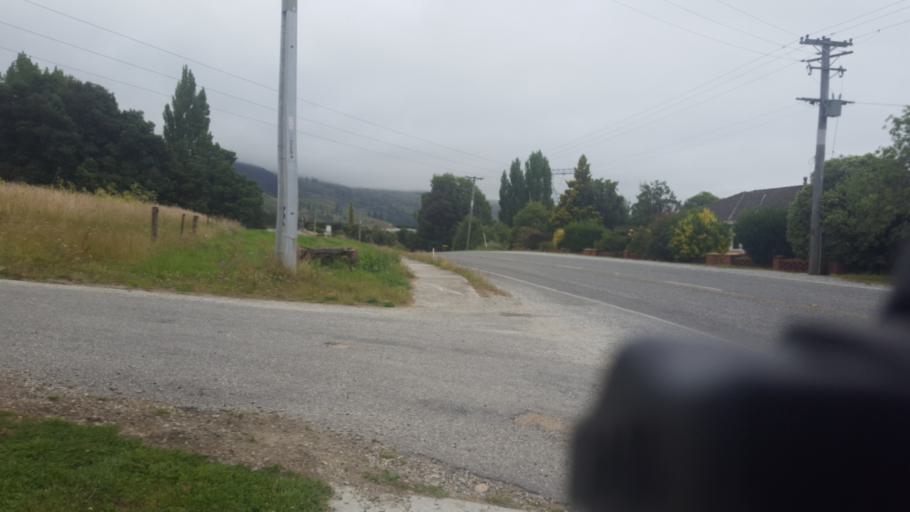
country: NZ
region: Otago
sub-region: Queenstown-Lakes District
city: Kingston
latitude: -45.5306
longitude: 169.2986
